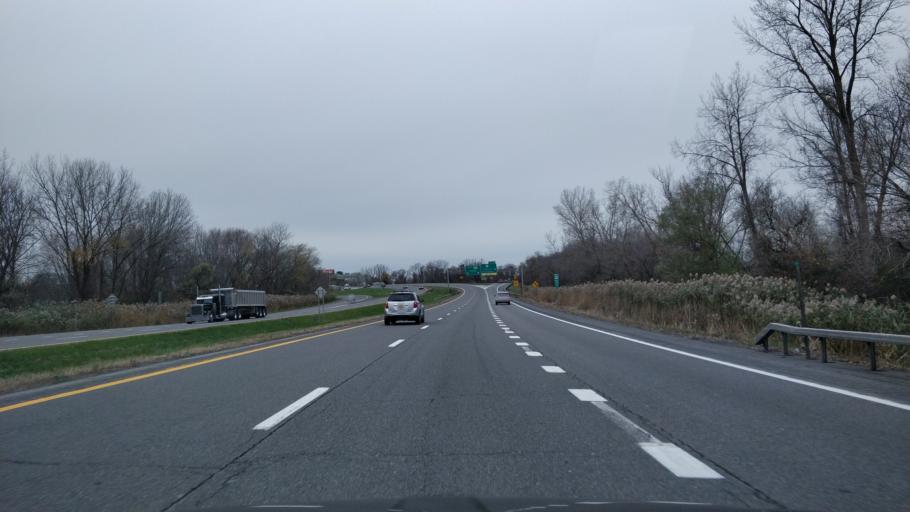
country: US
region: New York
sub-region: Onondaga County
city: North Syracuse
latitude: 43.1440
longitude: -76.1205
